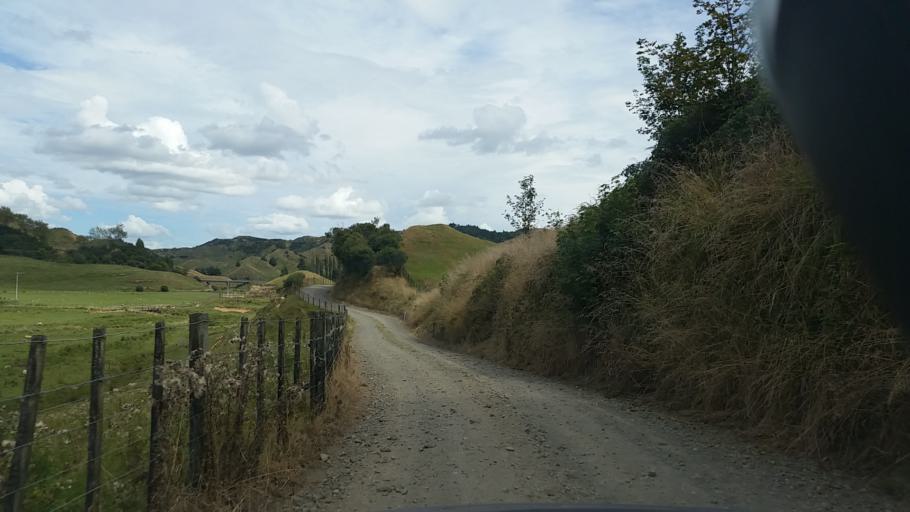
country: NZ
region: Taranaki
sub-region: South Taranaki District
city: Eltham
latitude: -39.2912
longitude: 174.4954
